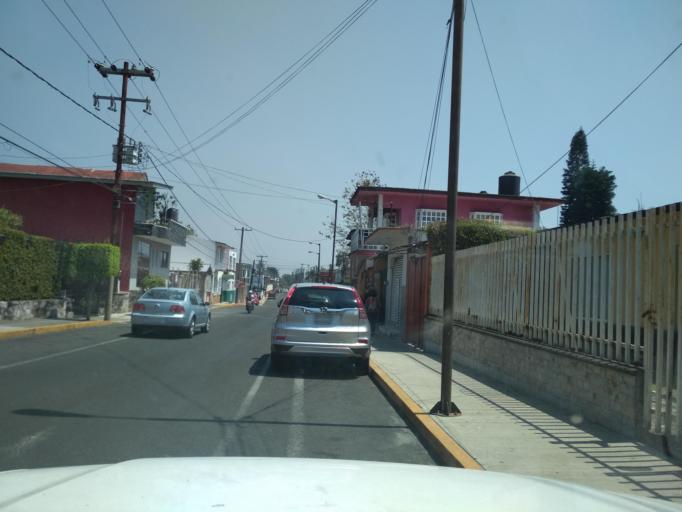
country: MX
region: Veracruz
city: Orizaba
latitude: 18.8516
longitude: -97.0894
